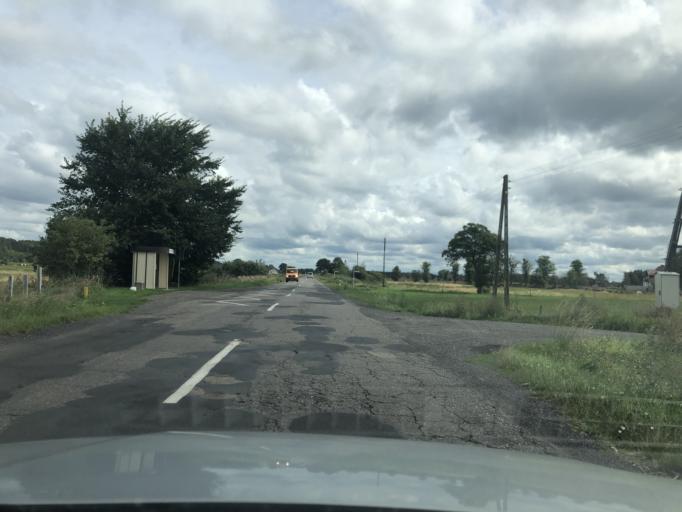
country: PL
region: Lubusz
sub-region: Powiat strzelecko-drezdenecki
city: Drezdenko
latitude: 52.8425
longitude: 15.8768
